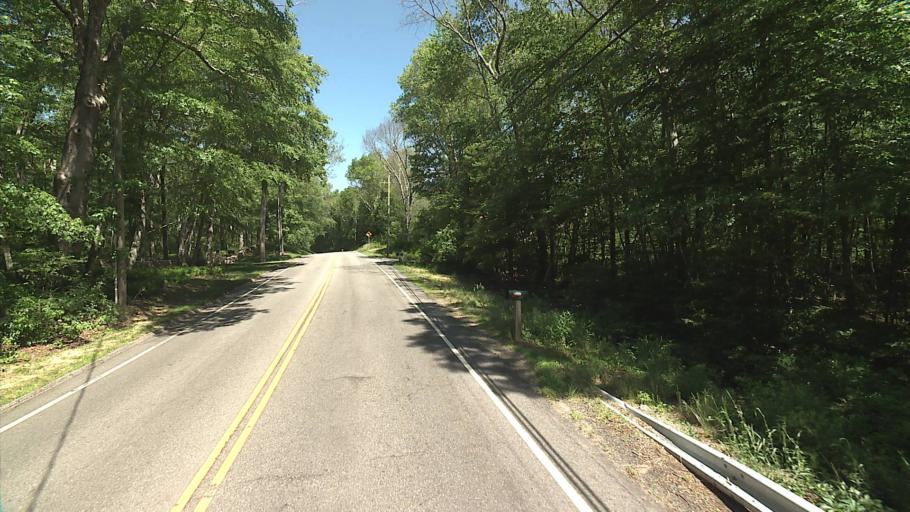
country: US
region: Rhode Island
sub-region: Washington County
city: Hopkinton
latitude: 41.4989
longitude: -71.8320
